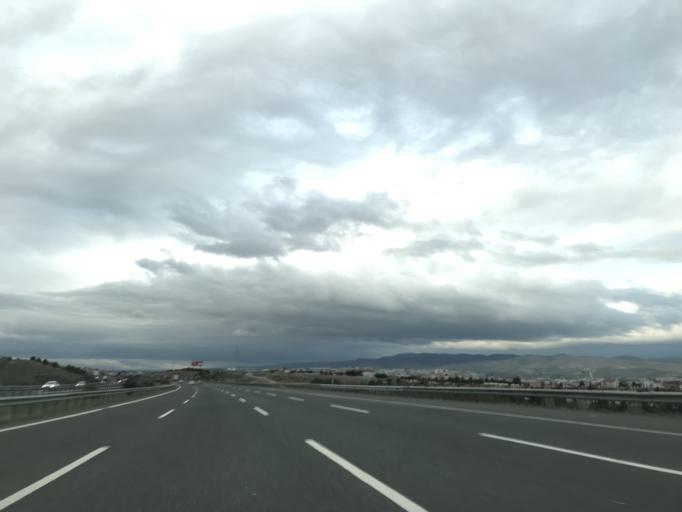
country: TR
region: Ankara
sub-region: Goelbasi
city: Golbasi
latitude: 39.7879
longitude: 32.7763
